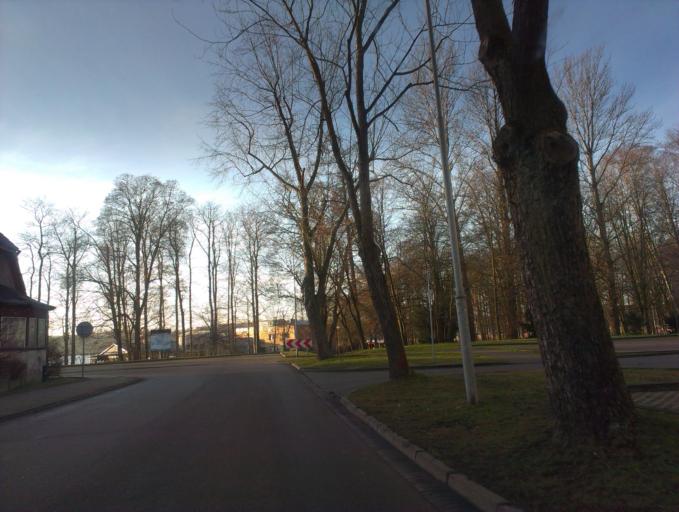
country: PL
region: West Pomeranian Voivodeship
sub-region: Powiat szczecinecki
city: Szczecinek
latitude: 53.7110
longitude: 16.6819
